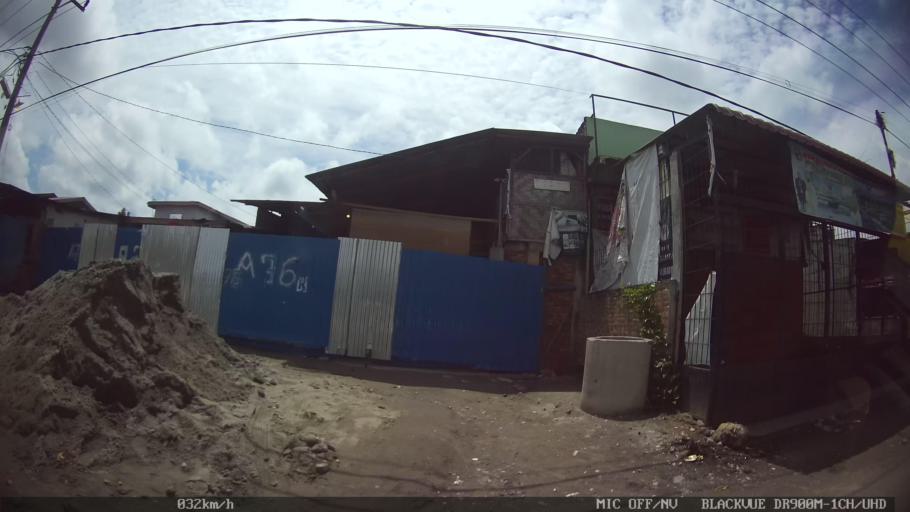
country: ID
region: North Sumatra
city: Medan
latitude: 3.6114
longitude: 98.7605
